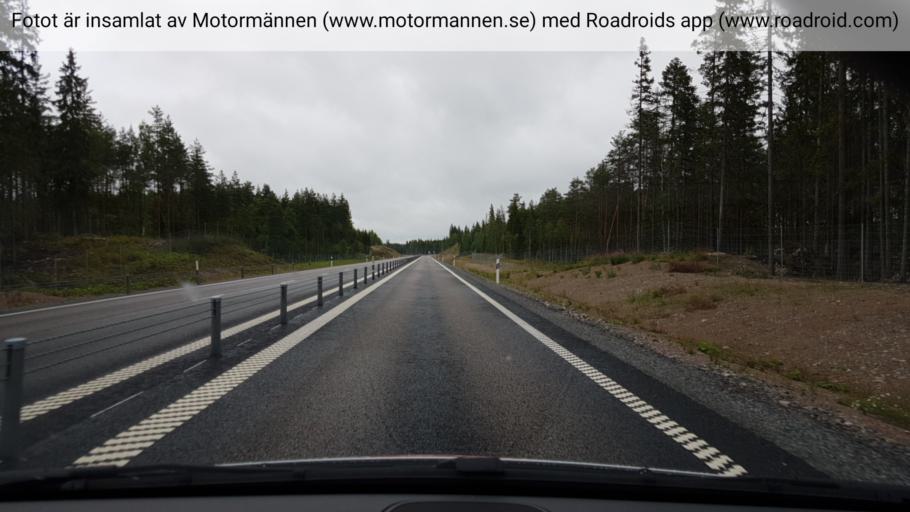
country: SE
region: Uppsala
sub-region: Heby Kommun
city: Tarnsjo
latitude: 60.1106
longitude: 16.9220
